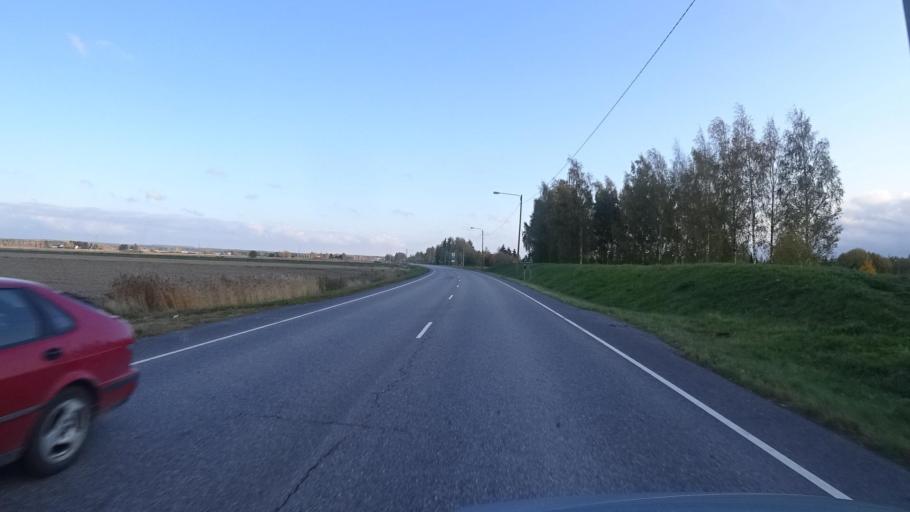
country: FI
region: Satakunta
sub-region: Rauma
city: Saekylae
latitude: 61.0561
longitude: 22.3307
